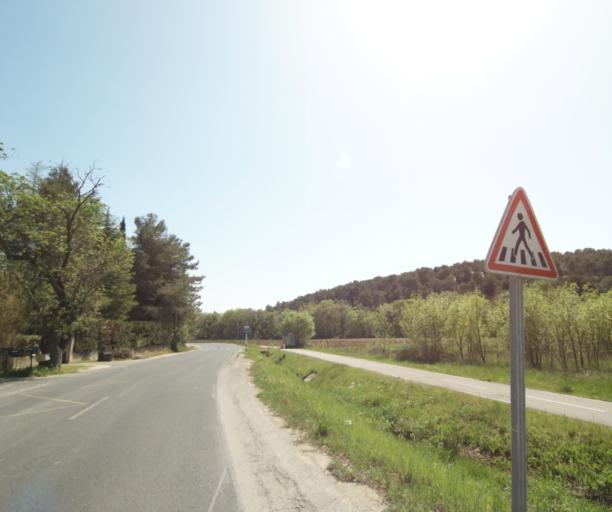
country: FR
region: Languedoc-Roussillon
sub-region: Departement de l'Herault
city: Montferrier-sur-Lez
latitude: 43.6622
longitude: 3.8472
